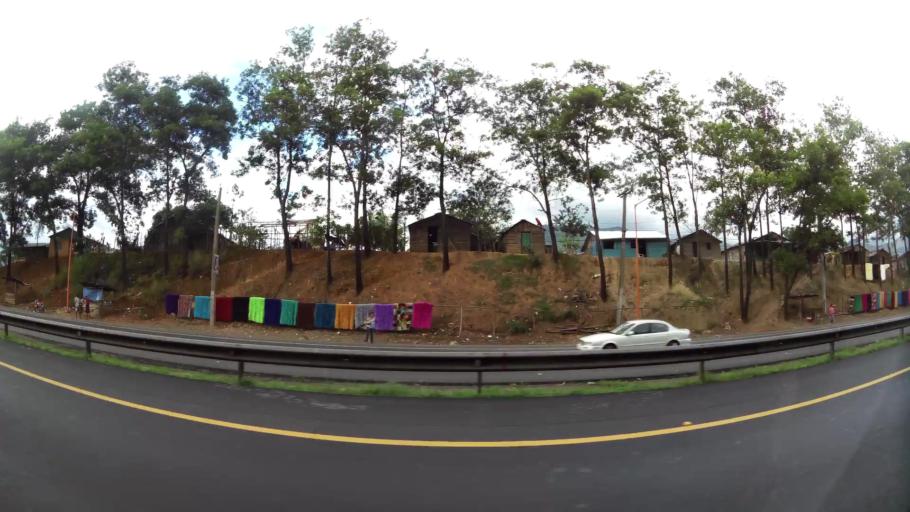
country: DO
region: Monsenor Nouel
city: Piedra Blanca
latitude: 18.8390
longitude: -70.3049
